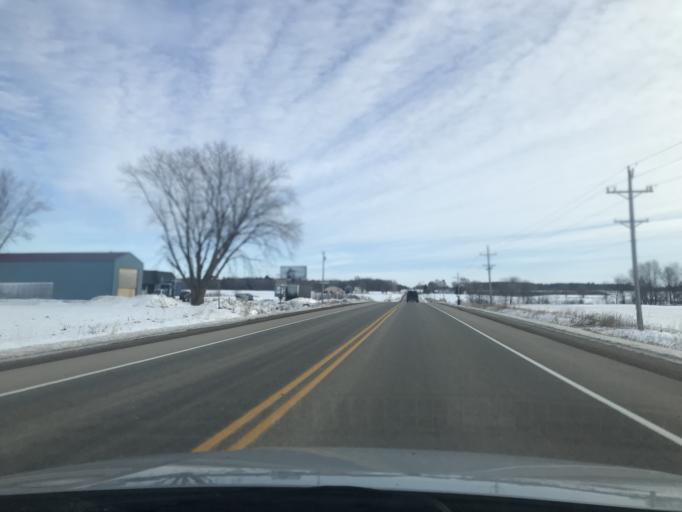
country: US
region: Wisconsin
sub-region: Oconto County
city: Oconto Falls
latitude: 44.8956
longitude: -88.2206
